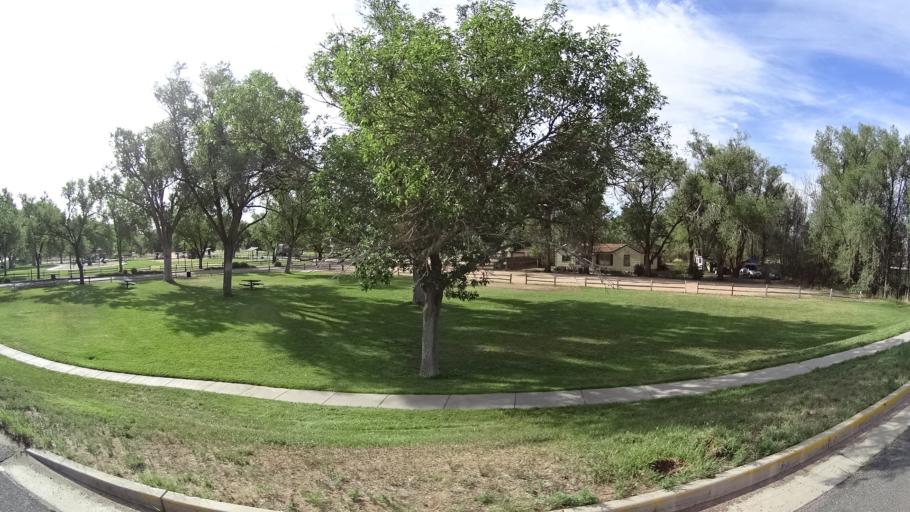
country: US
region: Colorado
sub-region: El Paso County
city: Fountain
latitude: 38.6836
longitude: -104.6938
